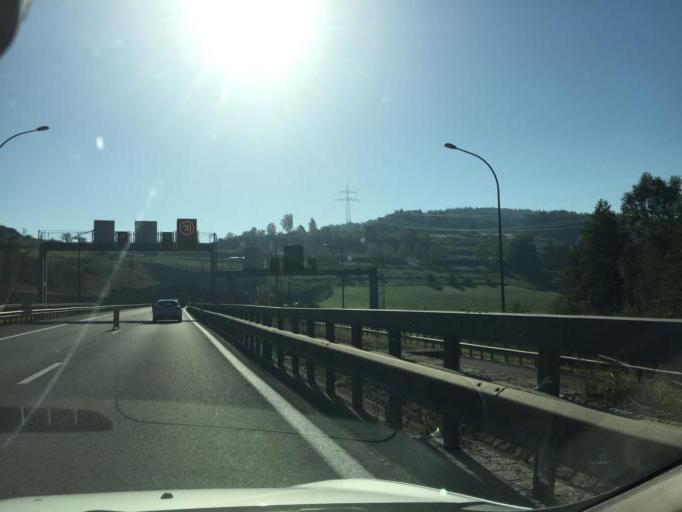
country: LU
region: Luxembourg
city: Rollingen
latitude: 49.7327
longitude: 6.1028
